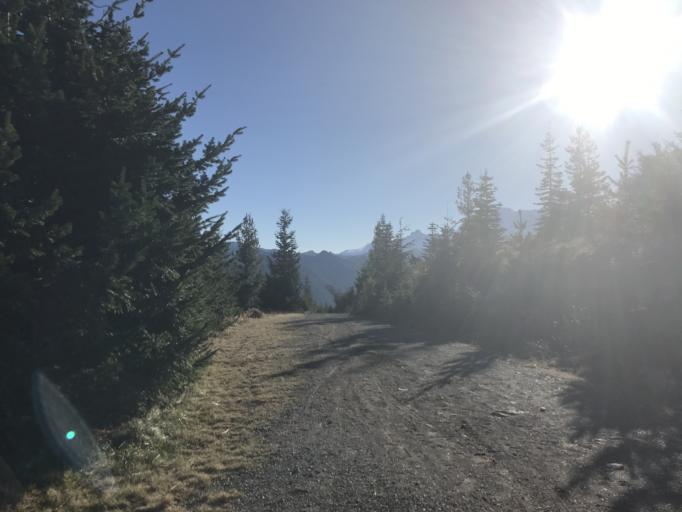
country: US
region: Washington
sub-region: King County
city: Enumclaw
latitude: 47.0410
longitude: -121.5962
